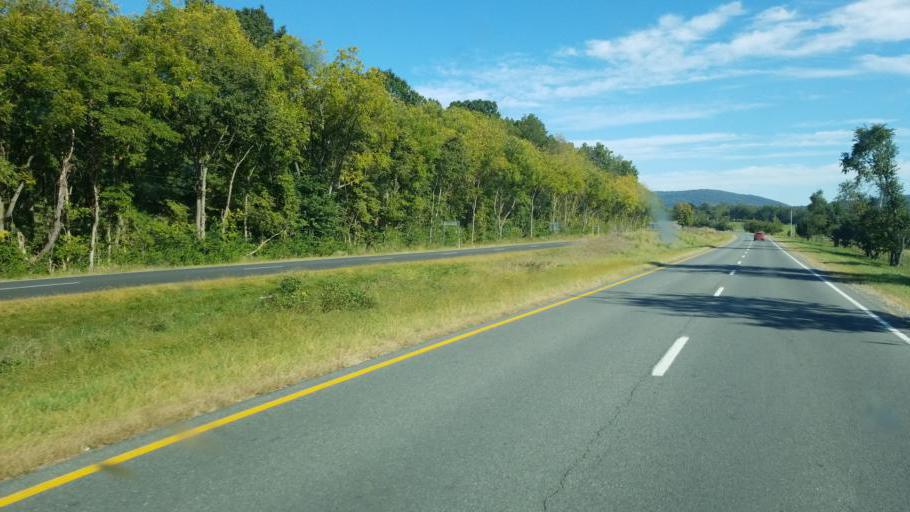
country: US
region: Virginia
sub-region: Warren County
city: Shenandoah Farms
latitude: 39.0578
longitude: -78.0391
